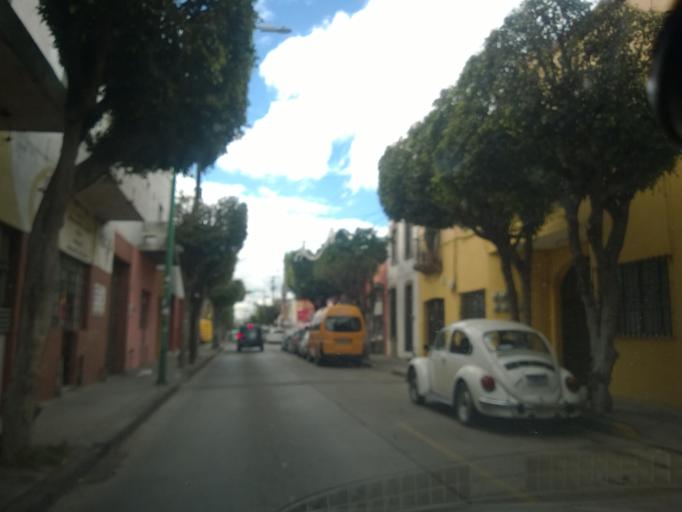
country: MX
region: Guanajuato
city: Leon
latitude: 21.1201
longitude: -101.6779
